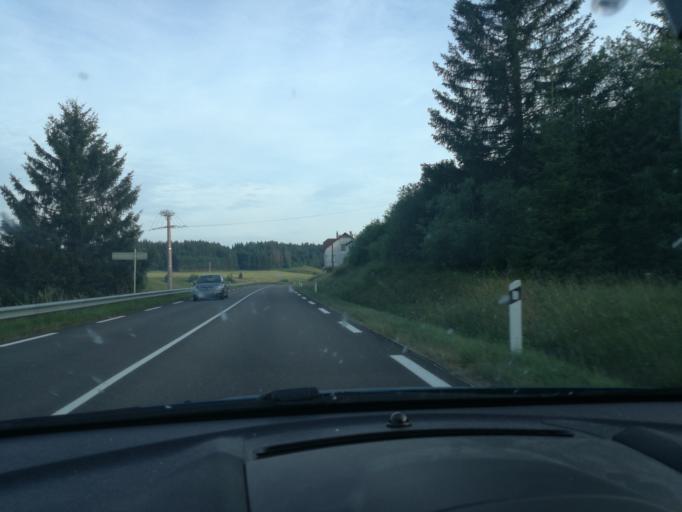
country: FR
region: Franche-Comte
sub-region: Departement du Jura
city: Morbier
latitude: 46.6060
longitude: 5.9623
